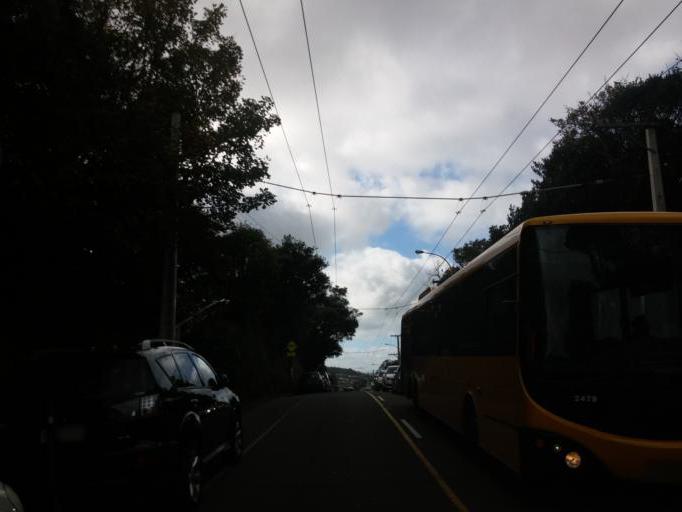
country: NZ
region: Wellington
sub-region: Wellington City
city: Kelburn
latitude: -41.2832
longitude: 174.7427
